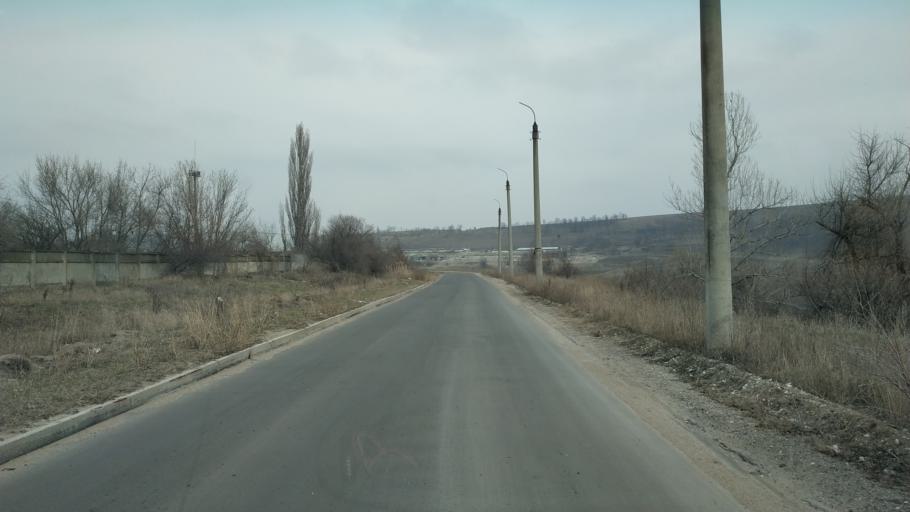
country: MD
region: Chisinau
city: Singera
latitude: 46.8964
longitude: 29.0203
